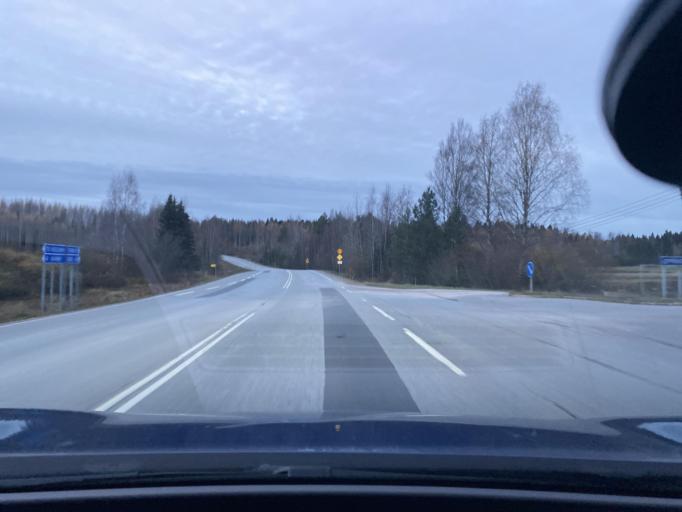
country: FI
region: Uusimaa
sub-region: Helsinki
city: Sammatti
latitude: 60.3899
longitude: 23.8116
